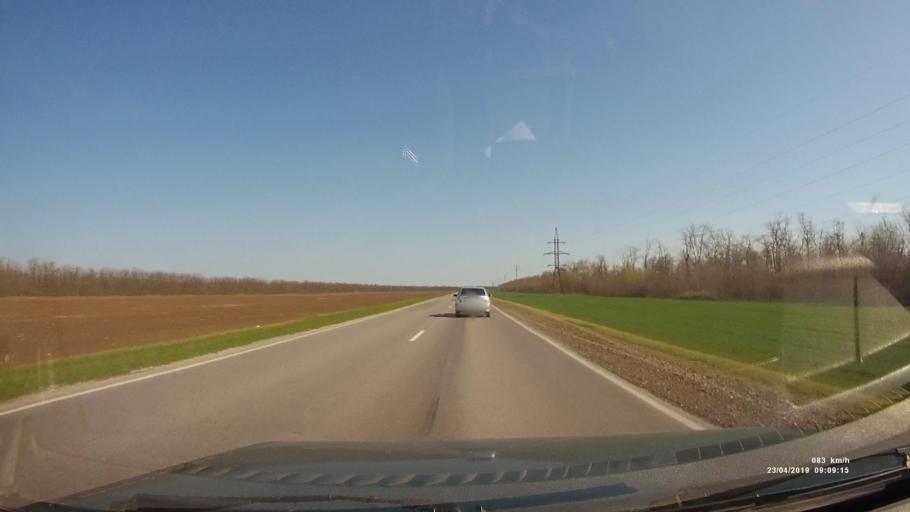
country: RU
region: Rostov
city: Sal'sk
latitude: 46.5714
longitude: 41.6134
